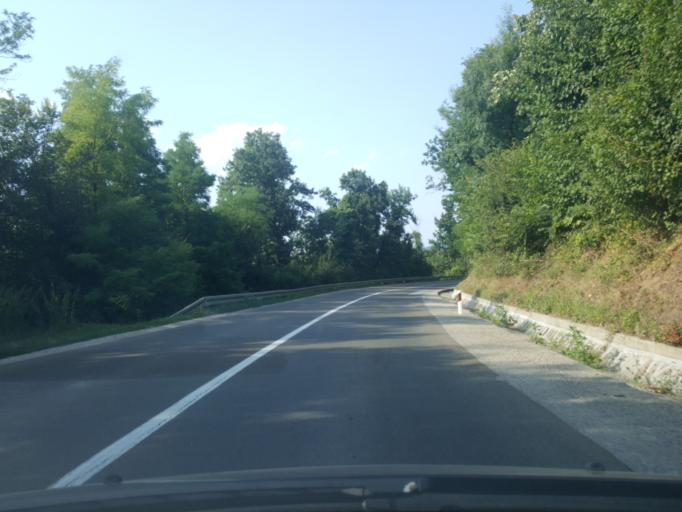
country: RS
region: Central Serbia
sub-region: Sumadijski Okrug
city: Topola
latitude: 44.2736
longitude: 20.6936
